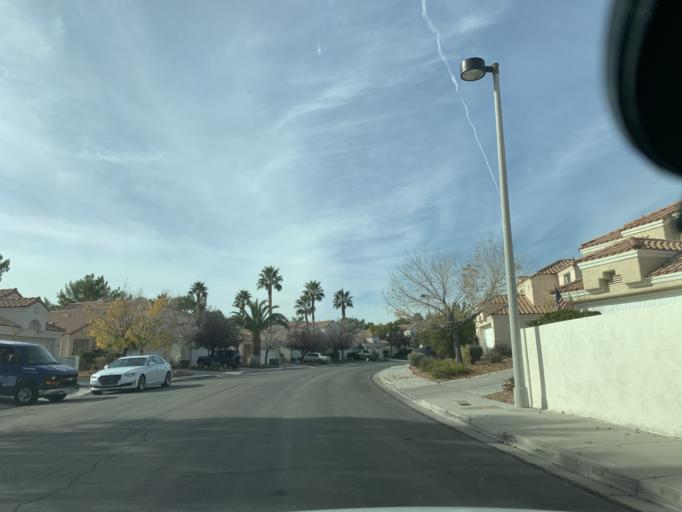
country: US
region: Nevada
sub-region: Clark County
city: Summerlin South
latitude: 36.1496
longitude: -115.2995
